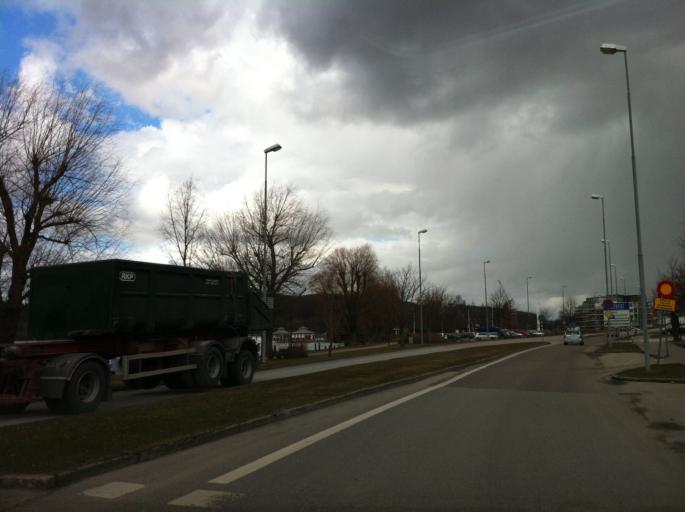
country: SE
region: Vaestra Goetaland
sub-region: Ulricehamns Kommun
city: Ulricehamn
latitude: 57.7272
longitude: 13.4350
